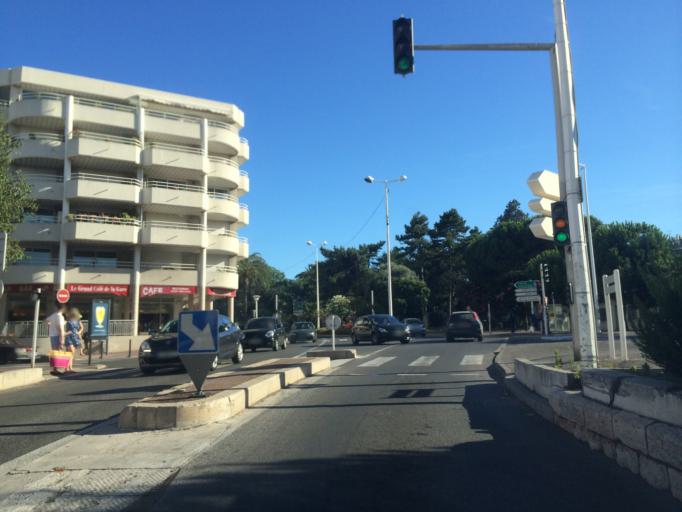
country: FR
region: Provence-Alpes-Cote d'Azur
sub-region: Departement des Alpes-Maritimes
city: Antibes
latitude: 43.5857
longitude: 7.1199
